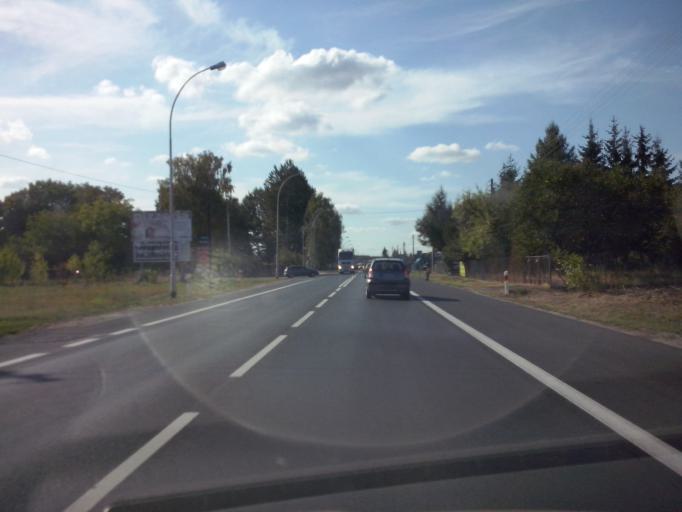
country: PL
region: Subcarpathian Voivodeship
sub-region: Powiat nizanski
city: Nisko
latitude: 50.5260
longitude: 22.1204
